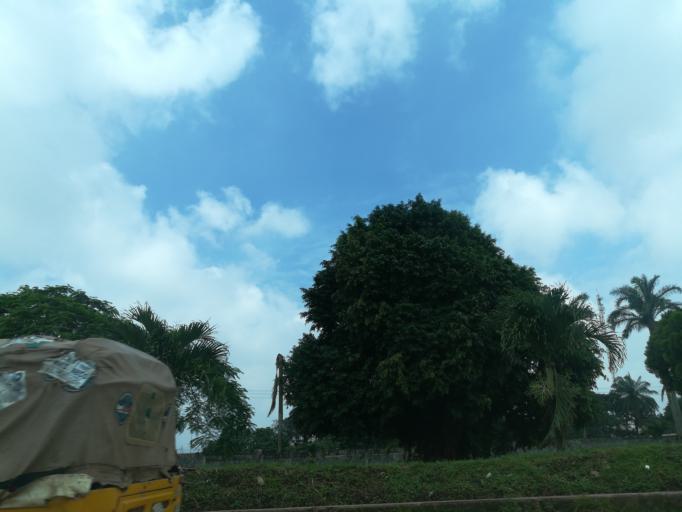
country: NG
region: Lagos
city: Ikorodu
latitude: 6.6760
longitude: 3.5126
